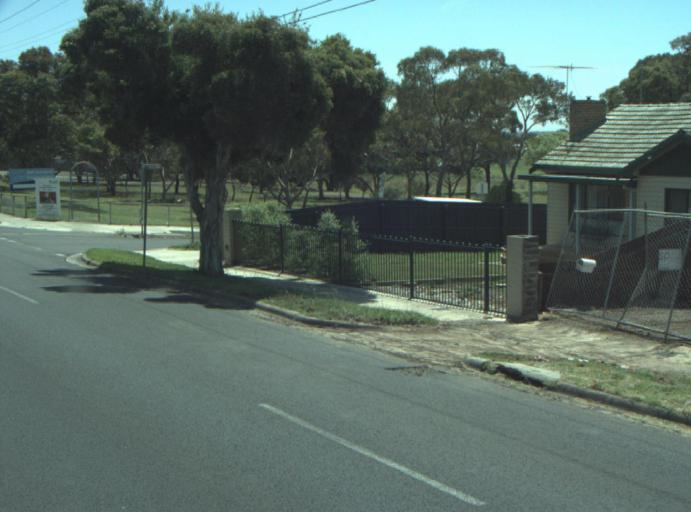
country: AU
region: Victoria
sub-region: Greater Geelong
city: Bell Park
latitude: -38.1062
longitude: 144.3324
